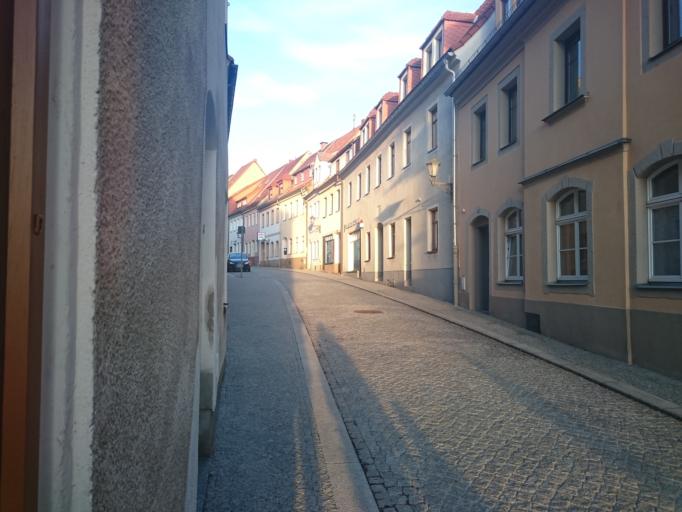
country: DE
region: Saxony
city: Dippoldiswalde
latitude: 50.8954
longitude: 13.6677
